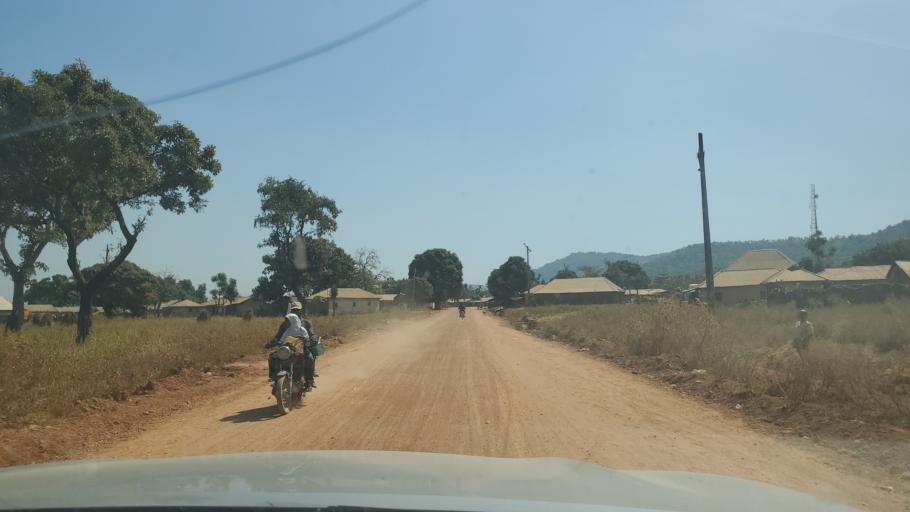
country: NG
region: Niger
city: Gawu Babangida
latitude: 9.2149
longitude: 6.8427
